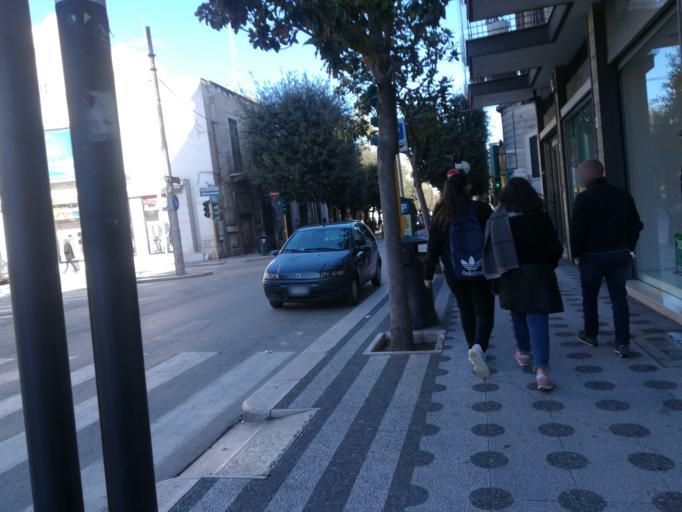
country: IT
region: Apulia
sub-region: Provincia di Barletta - Andria - Trani
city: Andria
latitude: 41.2293
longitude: 16.3016
